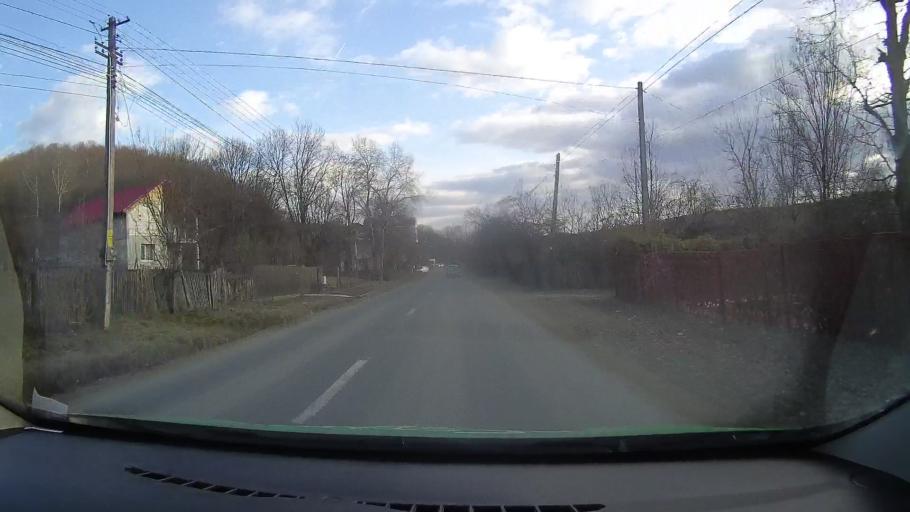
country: RO
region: Dambovita
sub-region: Comuna Ocnita
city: Ocnita
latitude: 44.9603
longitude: 25.5498
